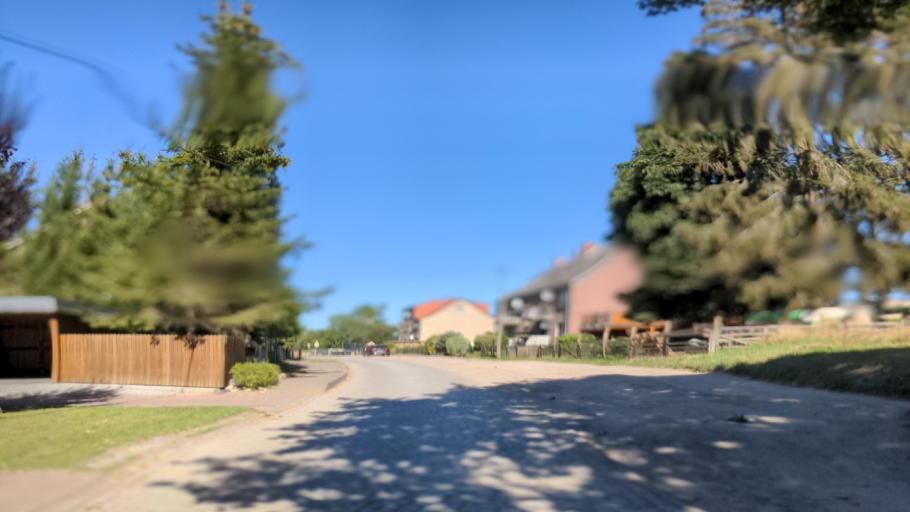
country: DE
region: Mecklenburg-Vorpommern
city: Selmsdorf
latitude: 53.8380
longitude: 10.8664
